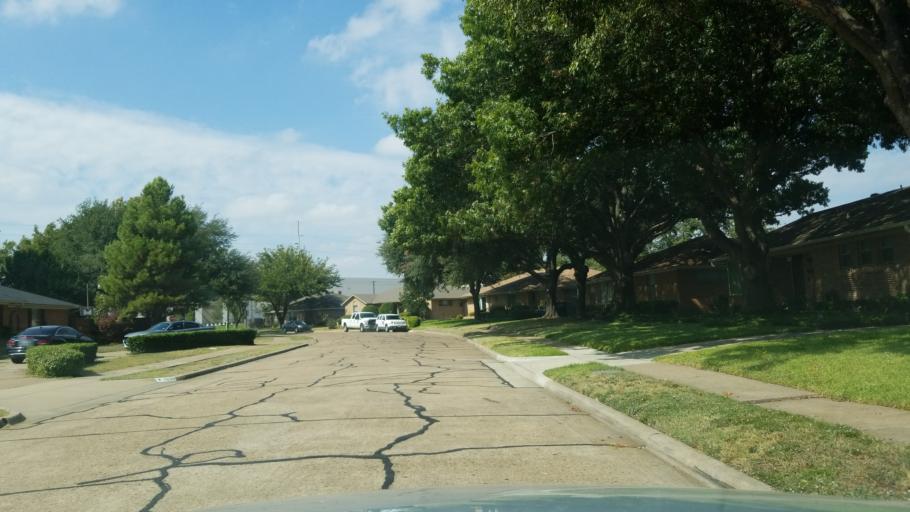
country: US
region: Texas
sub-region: Dallas County
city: Garland
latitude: 32.8962
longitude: -96.6646
